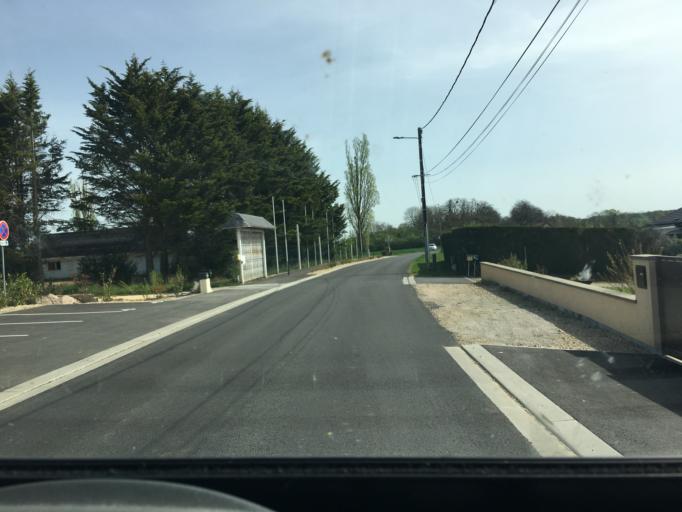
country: FR
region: Lorraine
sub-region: Departement de Meurthe-et-Moselle
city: Gondreville
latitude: 48.6605
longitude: 5.9833
